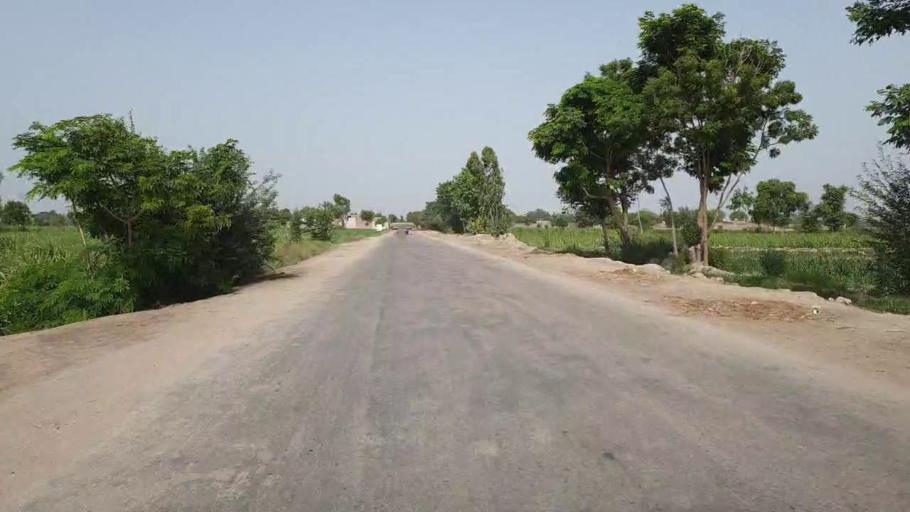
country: PK
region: Sindh
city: Daulatpur
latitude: 26.5604
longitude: 67.9762
